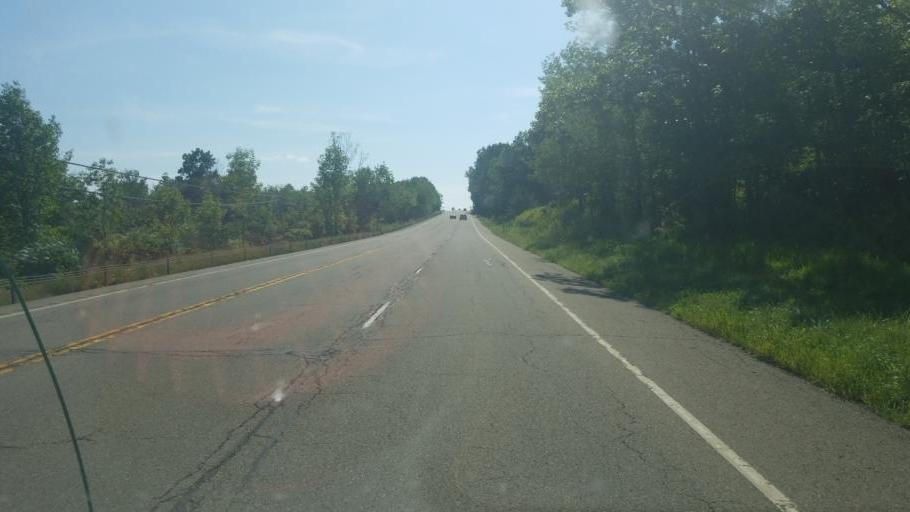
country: US
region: New York
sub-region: Allegany County
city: Wellsville
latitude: 42.1139
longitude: -78.0124
